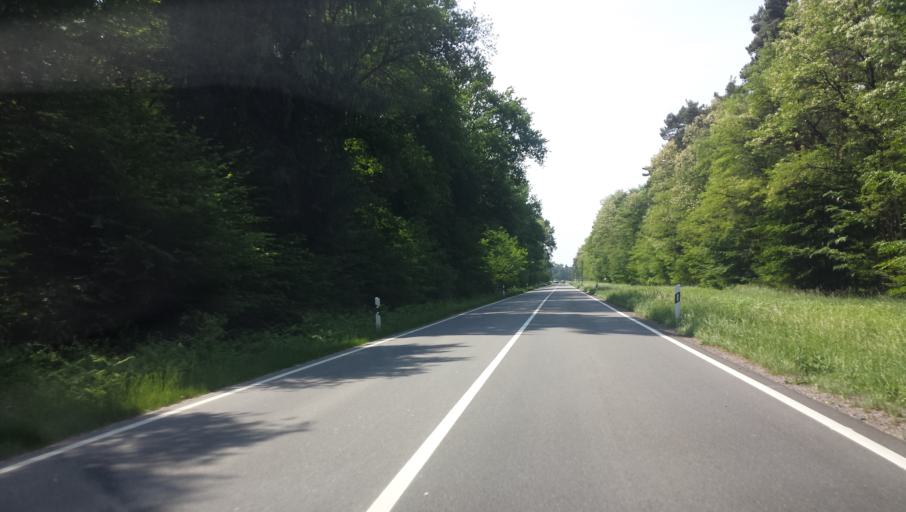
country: DE
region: Rheinland-Pfalz
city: Berg
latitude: 49.0028
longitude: 8.2169
